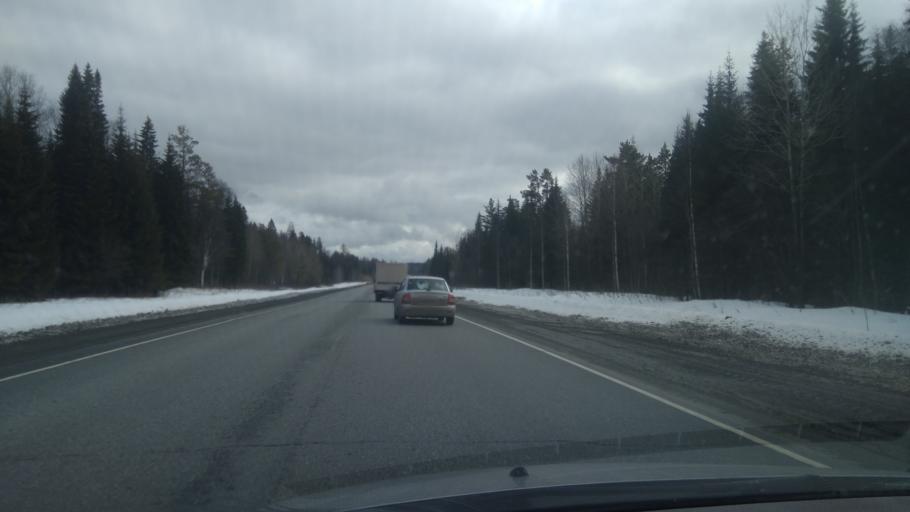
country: RU
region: Sverdlovsk
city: Atig
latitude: 56.8150
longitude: 59.3556
